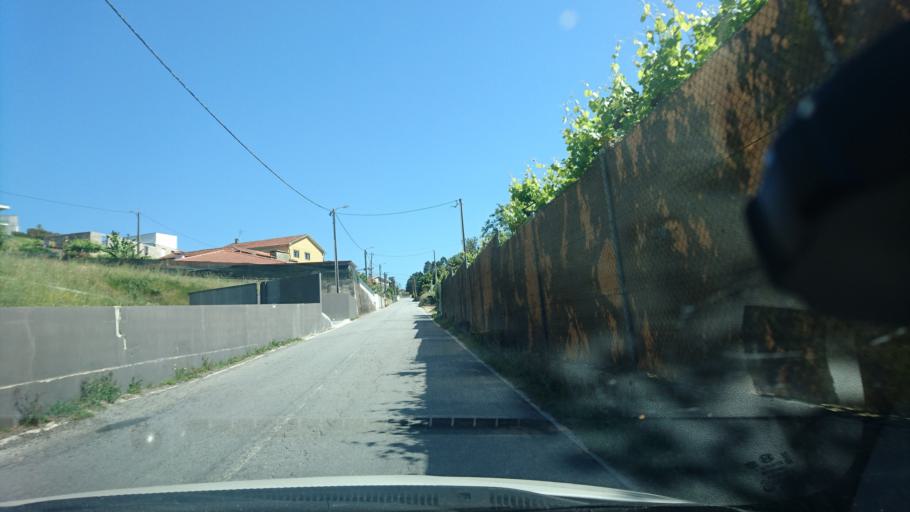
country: PT
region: Porto
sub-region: Paredes
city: Casteloes de Cepeda
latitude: 41.1805
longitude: -8.3360
